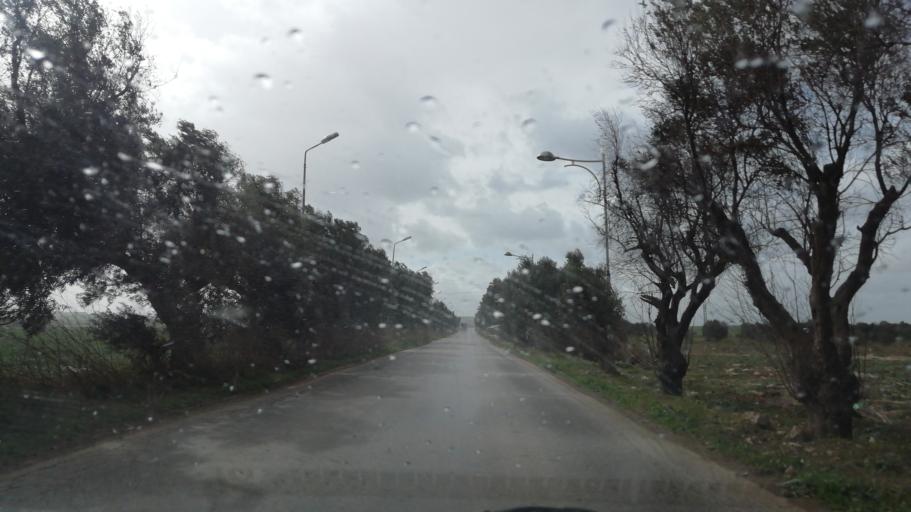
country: DZ
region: Oran
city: Sidi ech Chahmi
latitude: 35.6516
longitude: -0.5229
